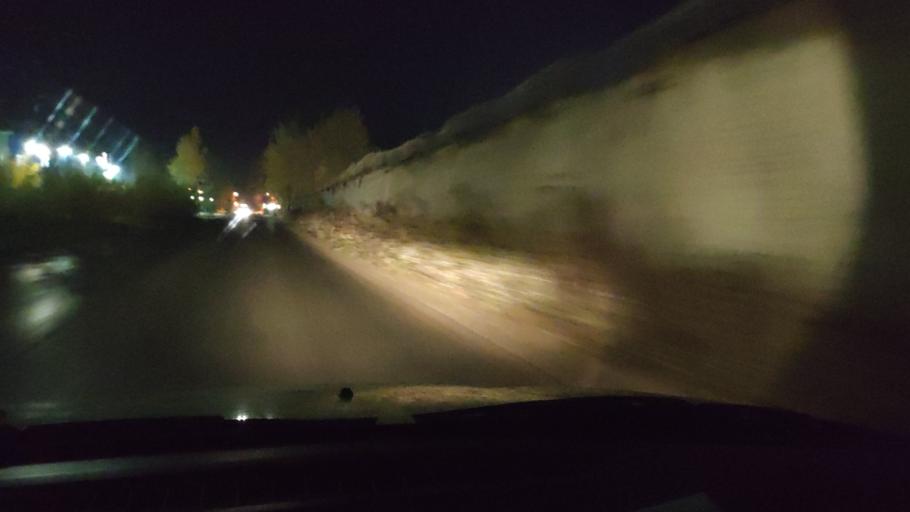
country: RU
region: Perm
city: Overyata
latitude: 58.0187
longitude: 55.9126
